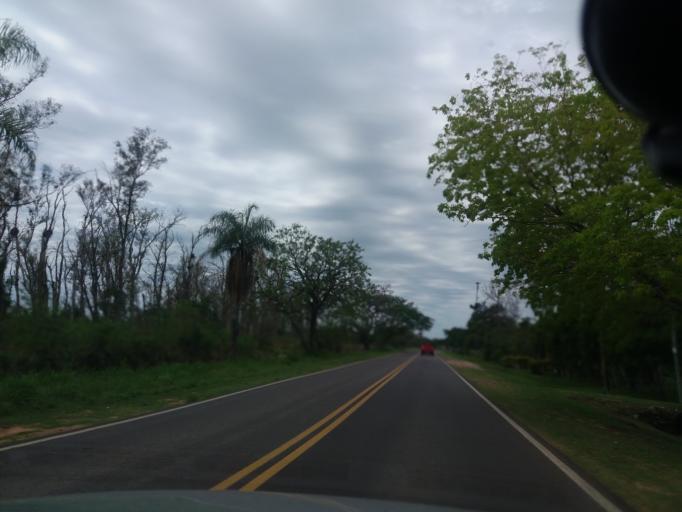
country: AR
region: Corrientes
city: Riachuelo
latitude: -27.4568
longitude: -58.7126
